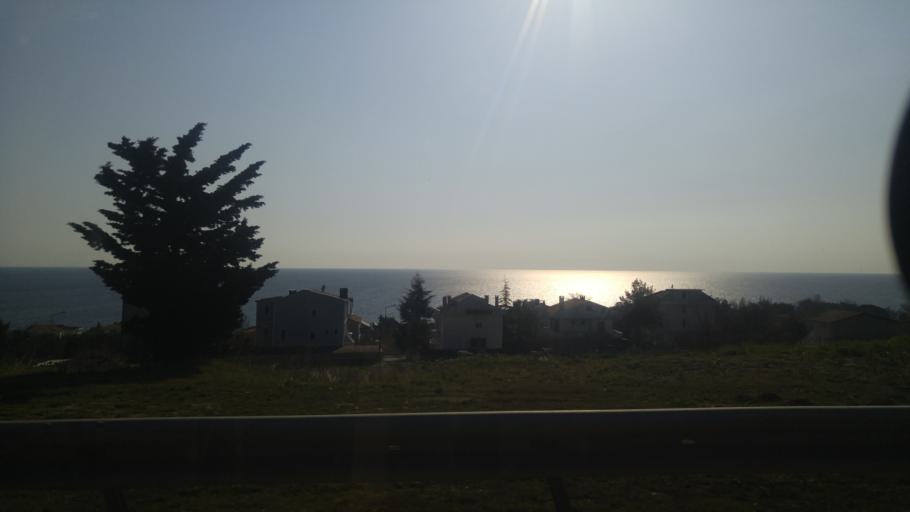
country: TR
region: Istanbul
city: Kumburgaz
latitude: 41.0141
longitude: 28.4923
